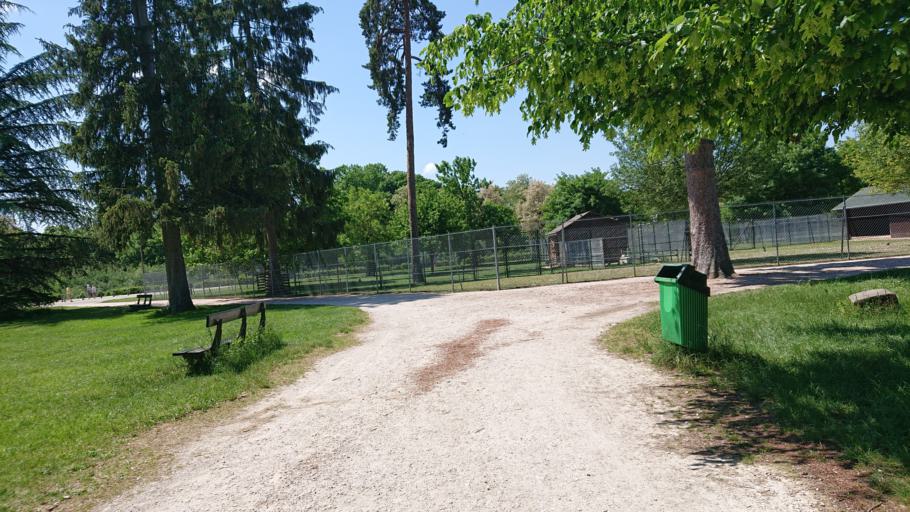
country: FR
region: Bourgogne
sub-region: Departement de la Cote-d'Or
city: Longvic
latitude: 47.2982
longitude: 5.0436
